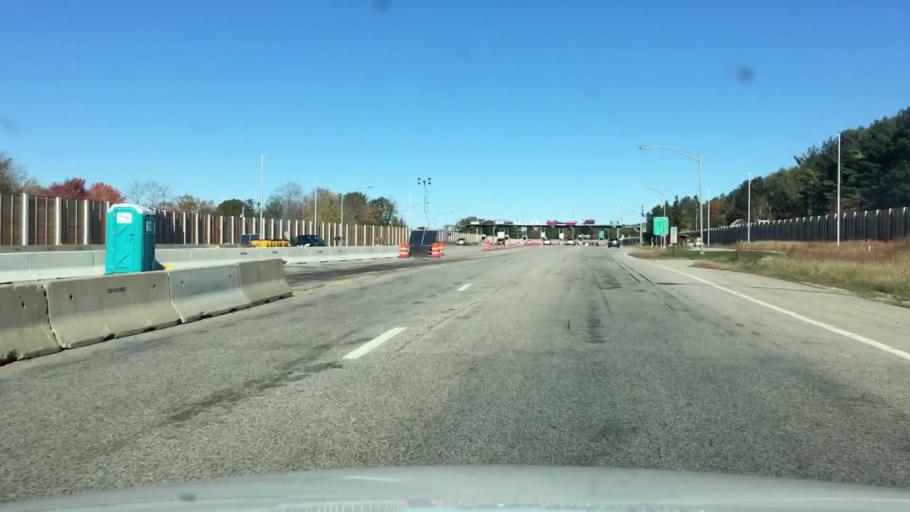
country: US
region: Maine
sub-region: York County
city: Eliot
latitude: 43.1347
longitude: -70.8404
